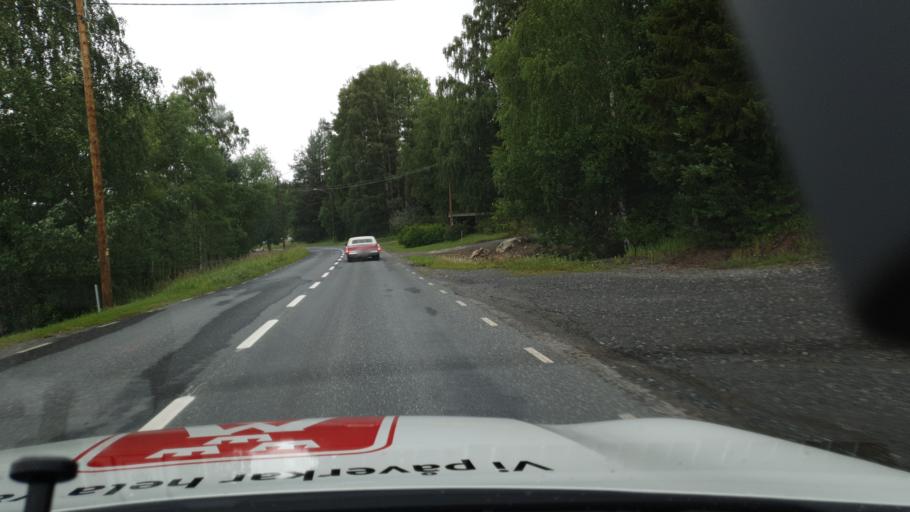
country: SE
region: Vaesterbotten
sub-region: Skelleftea Kommun
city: Forsbacka
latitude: 64.9121
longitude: 20.6181
